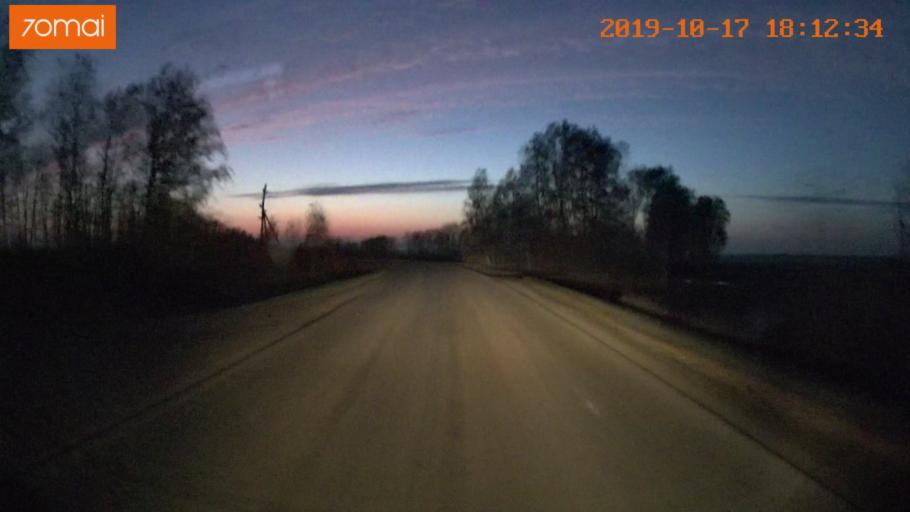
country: RU
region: Tula
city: Kurkino
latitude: 53.4120
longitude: 38.6086
